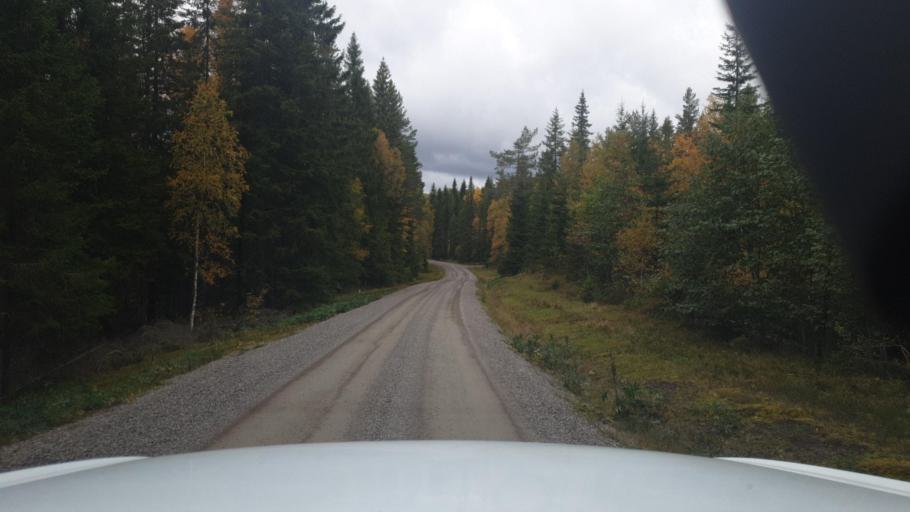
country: SE
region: Vaermland
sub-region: Eda Kommun
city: Charlottenberg
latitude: 60.0597
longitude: 12.6250
